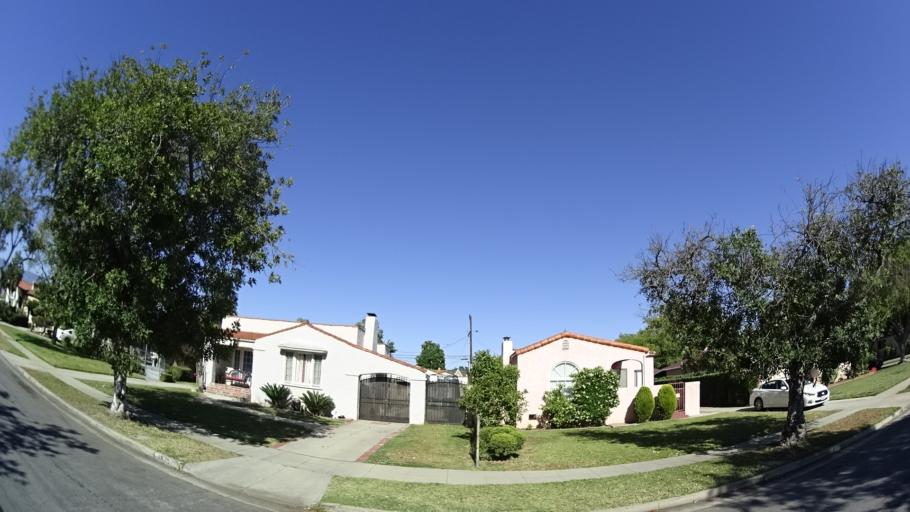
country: US
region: California
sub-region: Los Angeles County
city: Monterey Park
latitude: 34.0743
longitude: -118.1454
